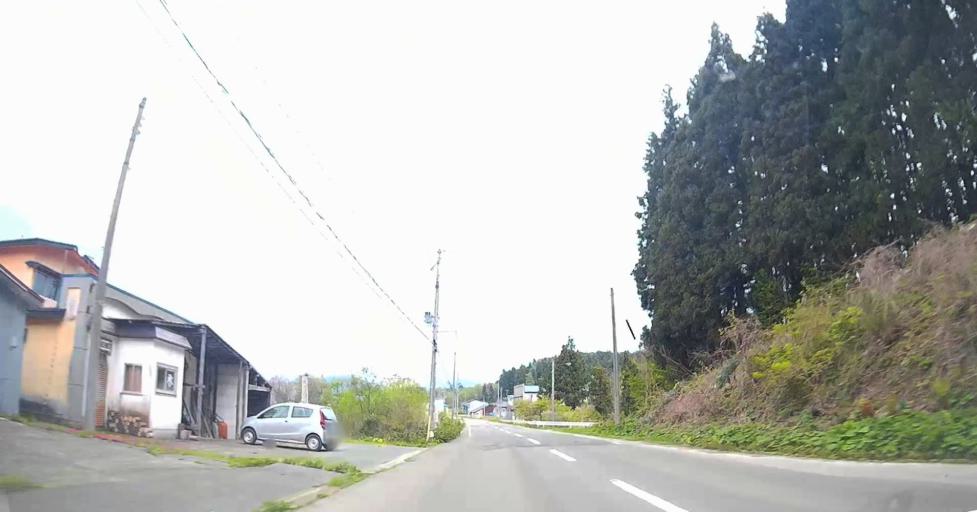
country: JP
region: Aomori
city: Shimokizukuri
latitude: 41.1798
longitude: 140.4631
